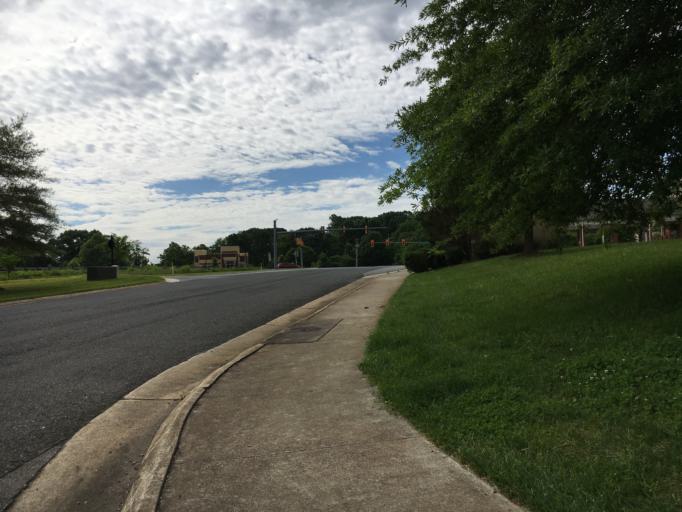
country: US
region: Virginia
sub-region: Bedford County
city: Forest
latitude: 37.3683
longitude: -79.2595
